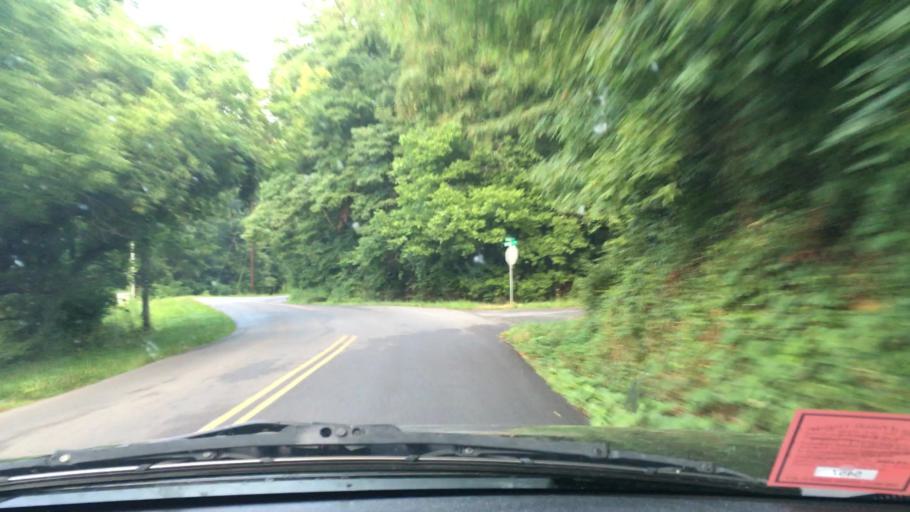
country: US
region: Virginia
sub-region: Pulaski County
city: Pulaski
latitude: 37.0431
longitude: -80.7562
